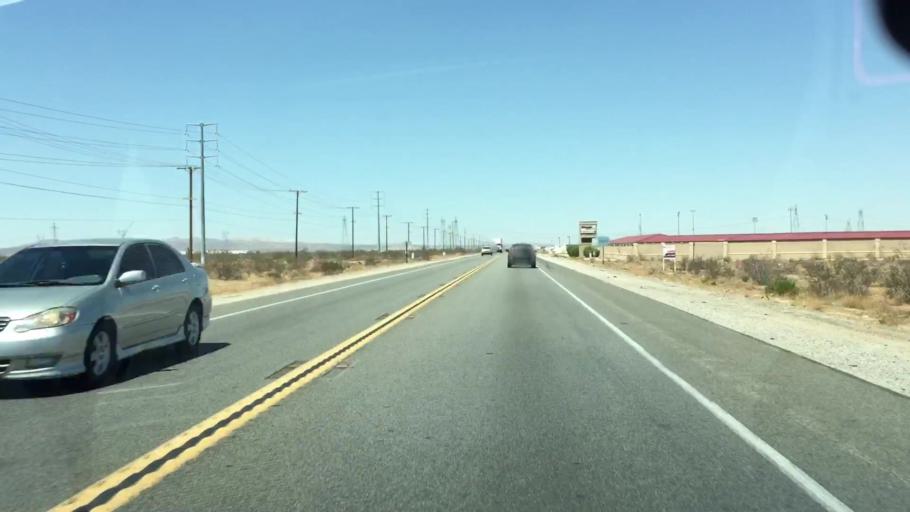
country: US
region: California
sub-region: San Bernardino County
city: Adelanto
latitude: 34.5473
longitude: -117.4012
